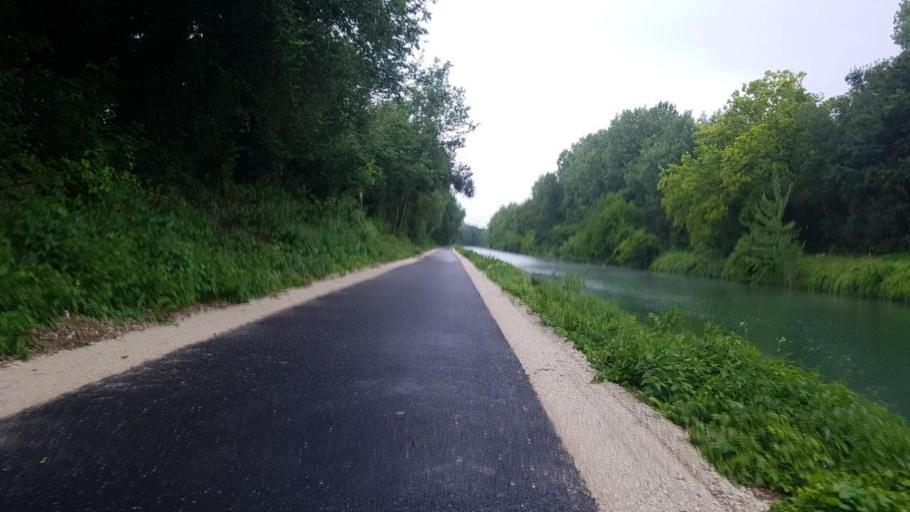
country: FR
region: Champagne-Ardenne
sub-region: Departement de la Marne
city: Sarry
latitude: 48.8671
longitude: 4.4641
